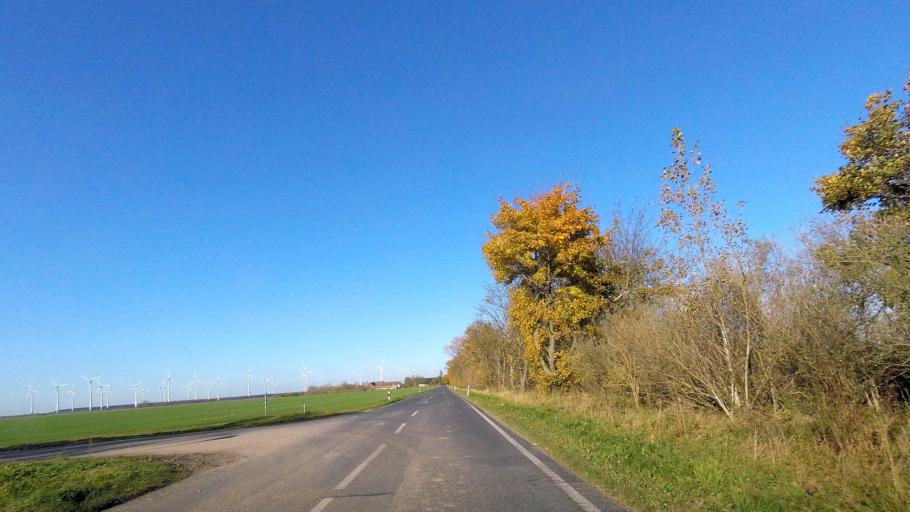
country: DE
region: Saxony-Anhalt
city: Zahna
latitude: 51.9871
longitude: 12.8591
